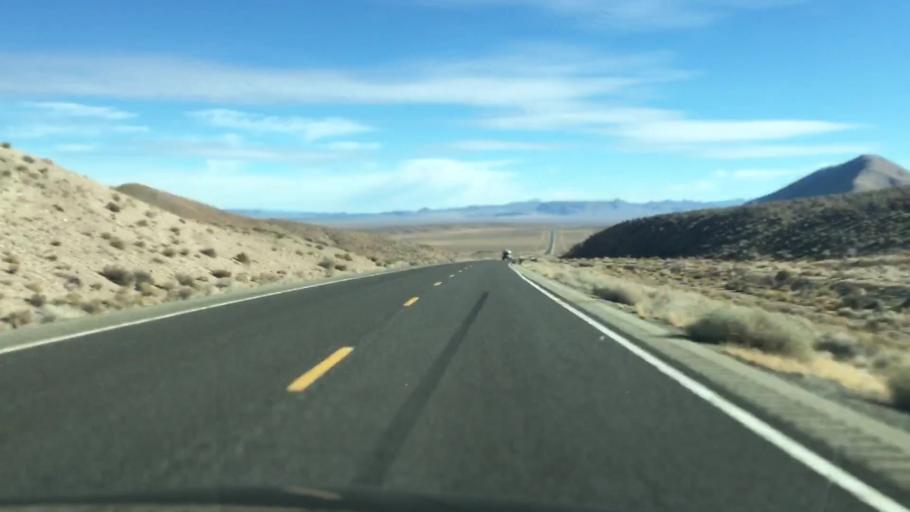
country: US
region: Nevada
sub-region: Lyon County
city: Yerington
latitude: 39.0365
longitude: -118.9292
